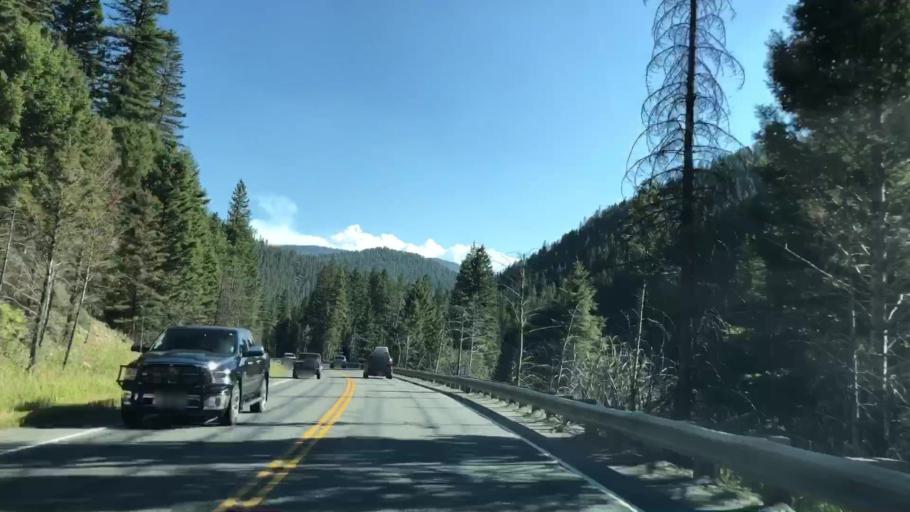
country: US
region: Montana
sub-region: Gallatin County
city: Big Sky
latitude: 45.3662
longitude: -111.1751
